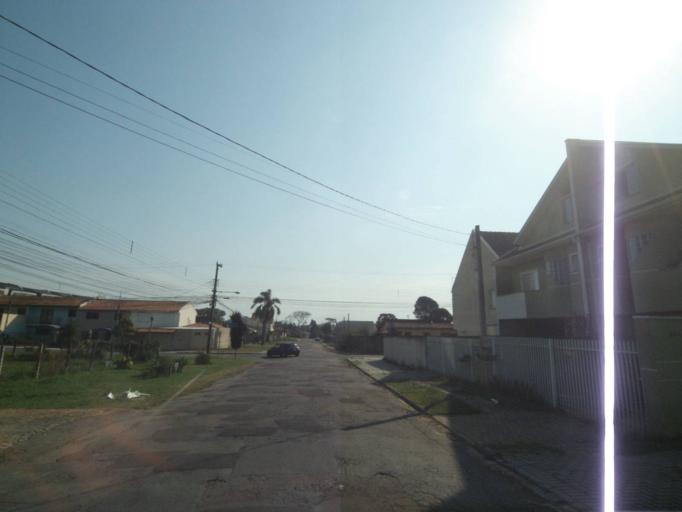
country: BR
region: Parana
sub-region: Sao Jose Dos Pinhais
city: Sao Jose dos Pinhais
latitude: -25.5079
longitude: -49.2559
